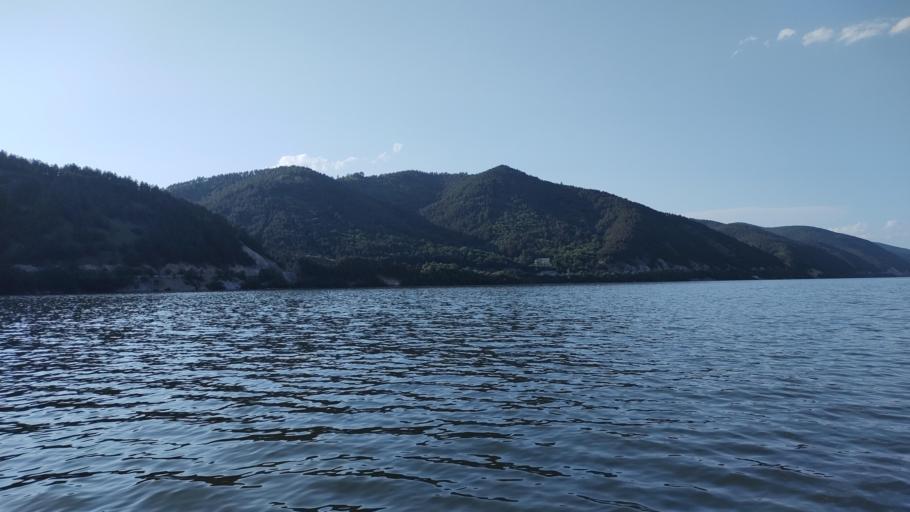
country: RO
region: Mehedinti
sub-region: Comuna Svinita
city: Svinita
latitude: 44.5119
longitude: 22.1990
